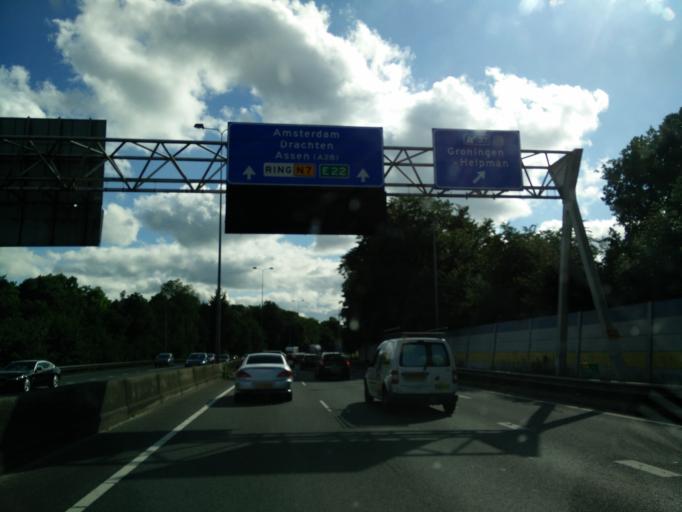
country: NL
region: Groningen
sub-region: Gemeente Groningen
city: Groningen
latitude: 53.2072
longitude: 6.5791
